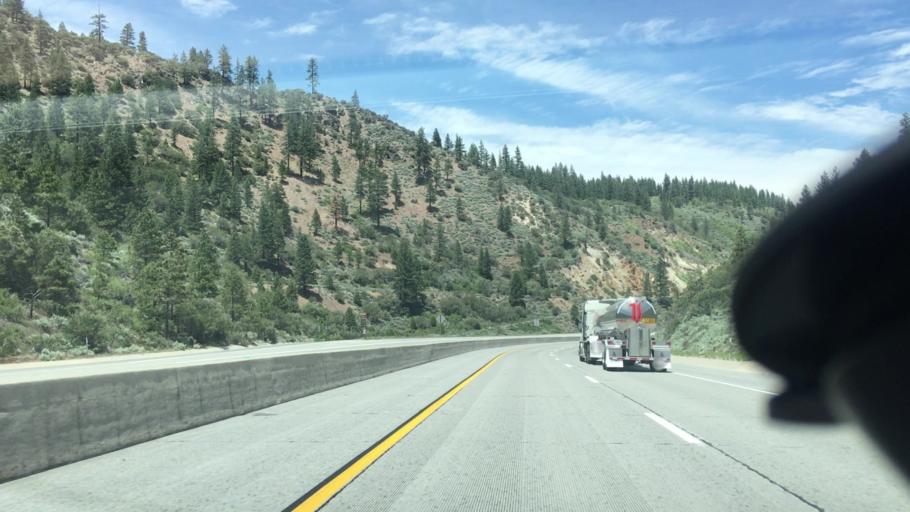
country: US
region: Nevada
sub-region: Washoe County
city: Verdi
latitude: 39.3915
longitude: -120.0253
